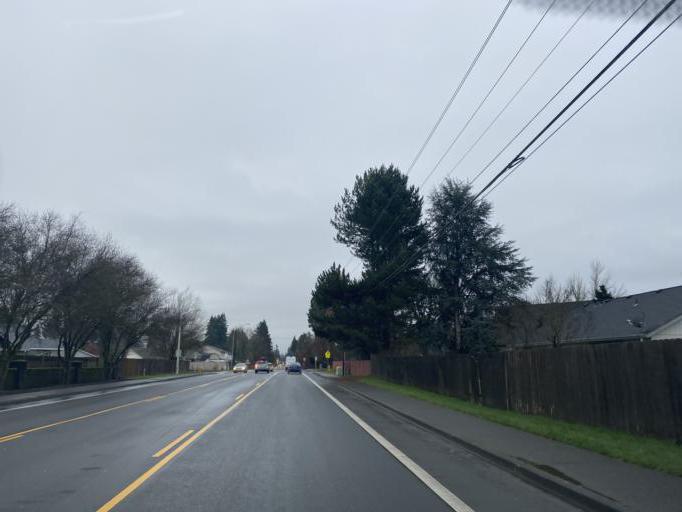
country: US
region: Washington
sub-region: Clark County
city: Battle Ground
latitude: 45.7759
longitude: -122.5375
